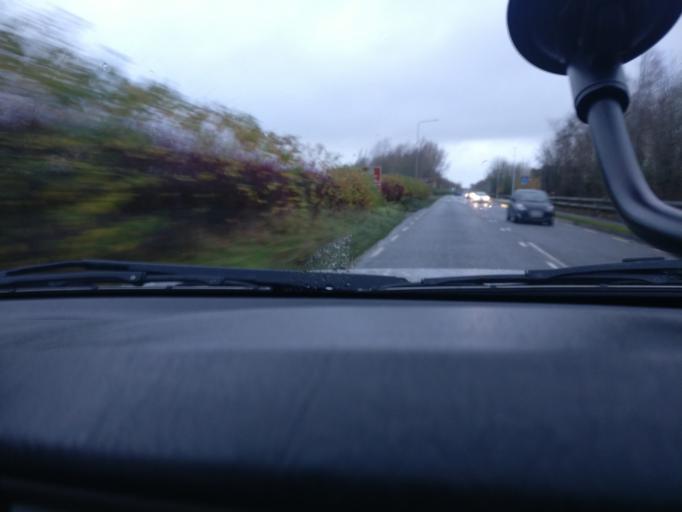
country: IE
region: Leinster
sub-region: An Iarmhi
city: Kinnegad
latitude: 53.4523
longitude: -7.0983
